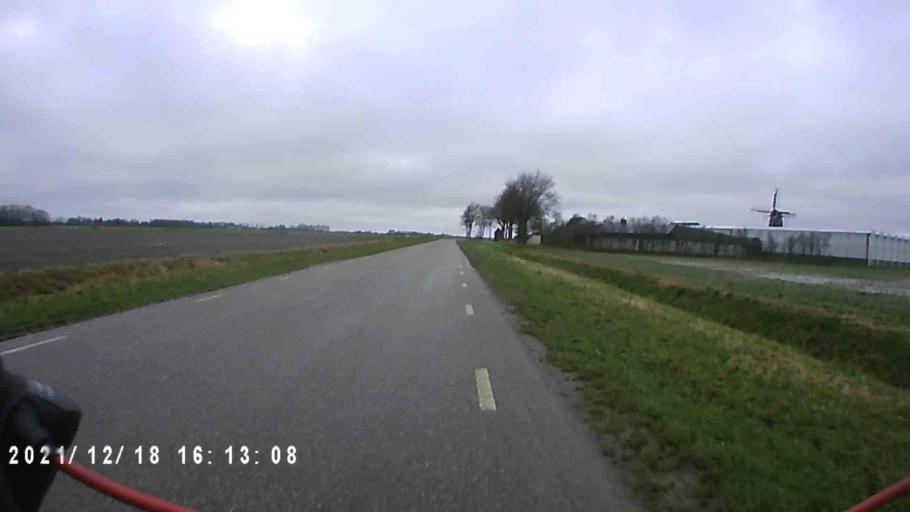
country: NL
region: Friesland
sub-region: Gemeente Dongeradeel
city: Anjum
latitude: 53.3673
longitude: 6.0687
